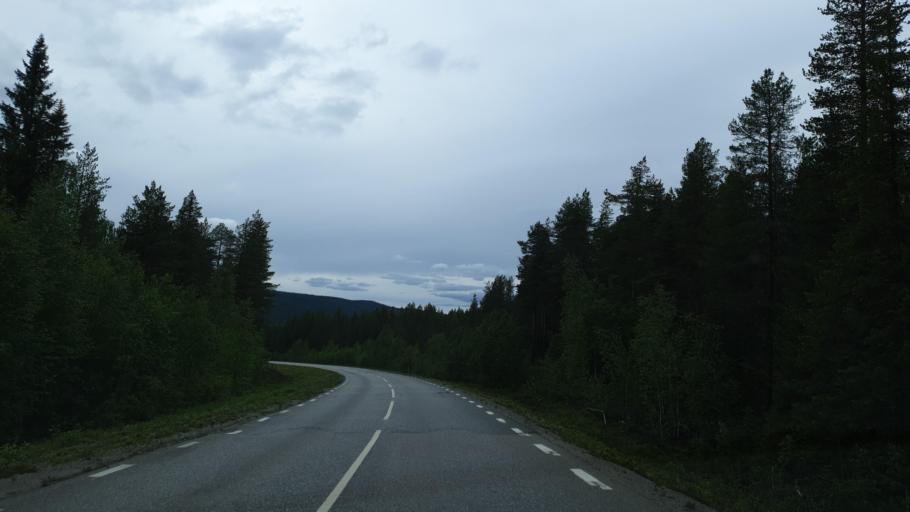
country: SE
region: Vaesterbotten
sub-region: Sorsele Kommun
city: Sorsele
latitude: 65.5445
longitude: 17.4516
